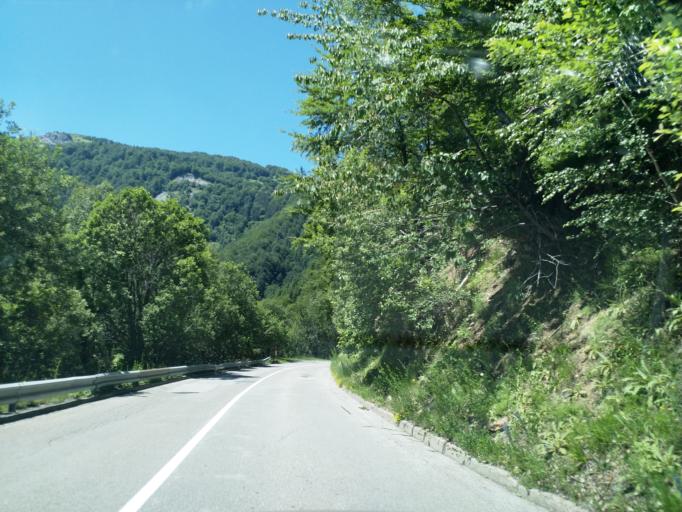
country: XK
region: Mitrovica
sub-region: Komuna e Leposaviqit
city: Leposaviq
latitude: 43.3095
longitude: 20.8615
